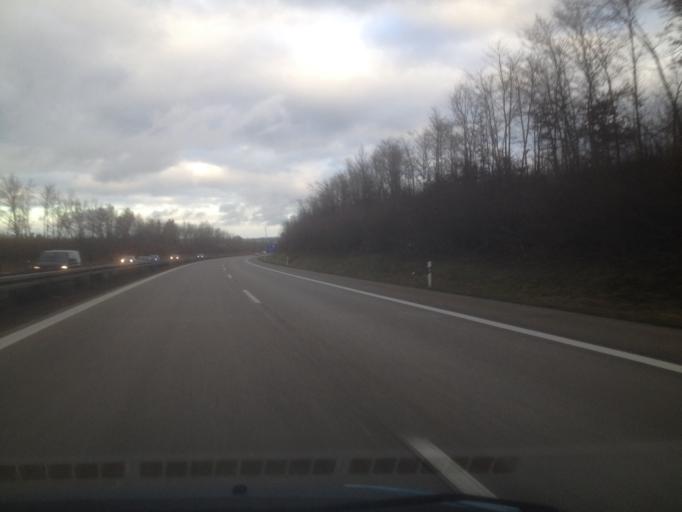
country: DE
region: Baden-Wuerttemberg
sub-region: Regierungsbezirk Stuttgart
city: Ellenberg
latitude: 49.1028
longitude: 10.2161
